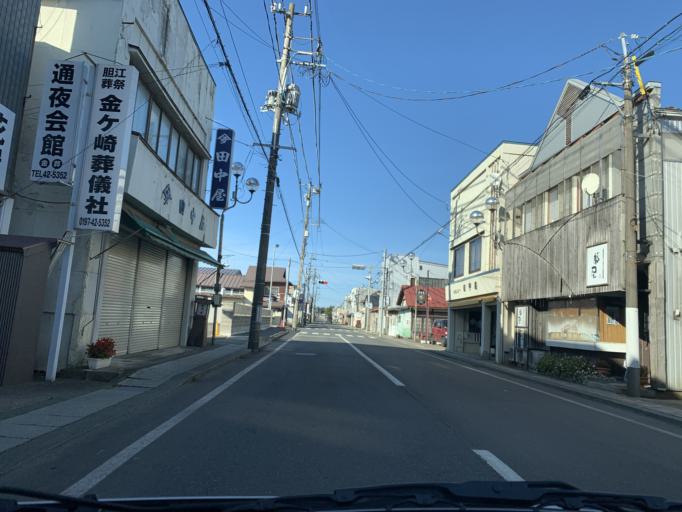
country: JP
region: Iwate
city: Mizusawa
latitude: 39.1968
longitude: 141.1183
